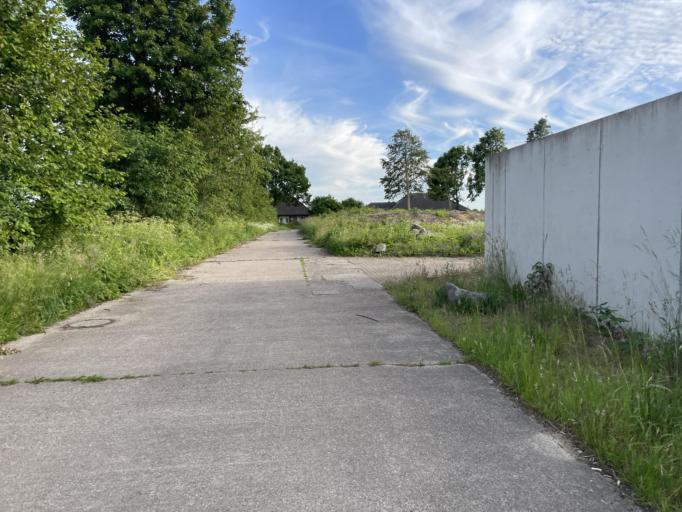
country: DE
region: Schleswig-Holstein
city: Mildstedt
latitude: 54.4627
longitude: 9.1090
